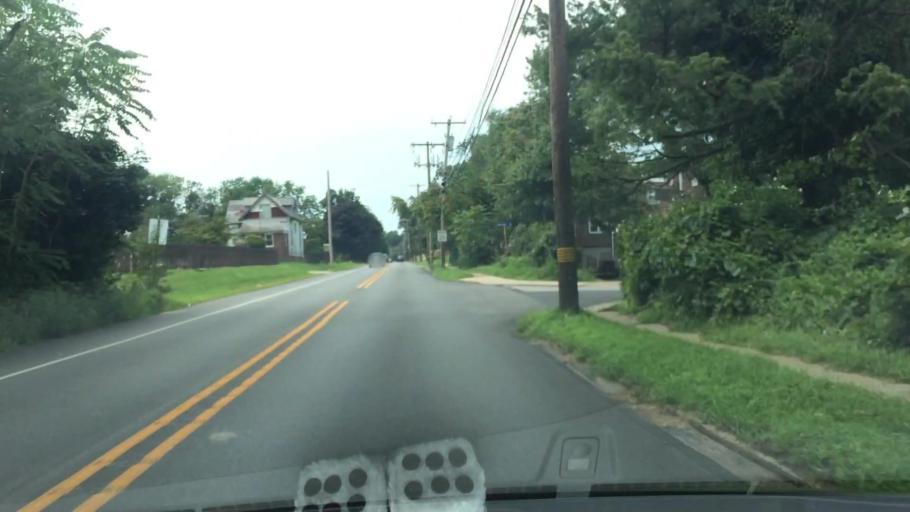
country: US
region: Pennsylvania
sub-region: Delaware County
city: Darby
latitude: 39.9197
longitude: -75.2695
